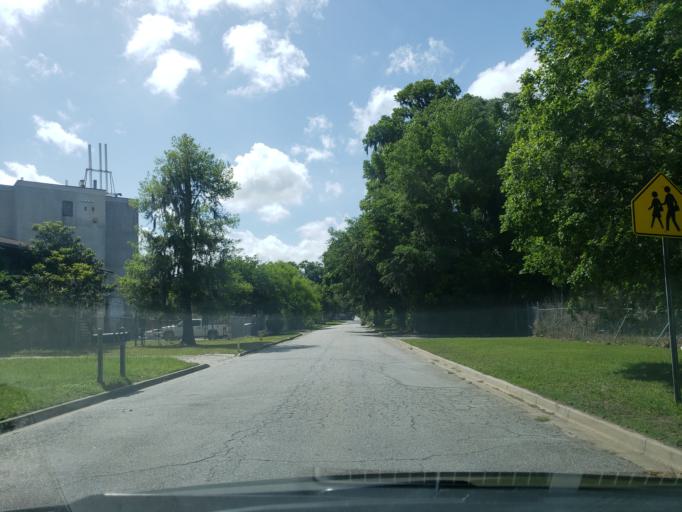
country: US
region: Georgia
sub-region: Chatham County
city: Thunderbolt
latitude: 32.0191
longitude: -81.0654
